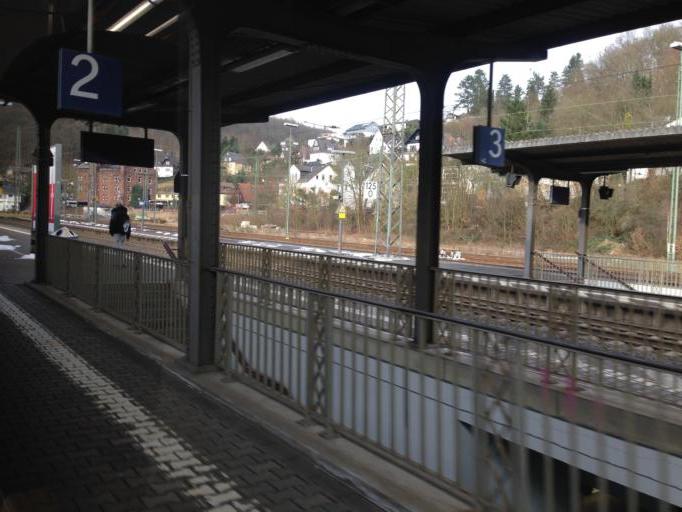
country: DE
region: Hesse
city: Dillenburg
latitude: 50.7352
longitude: 8.2945
